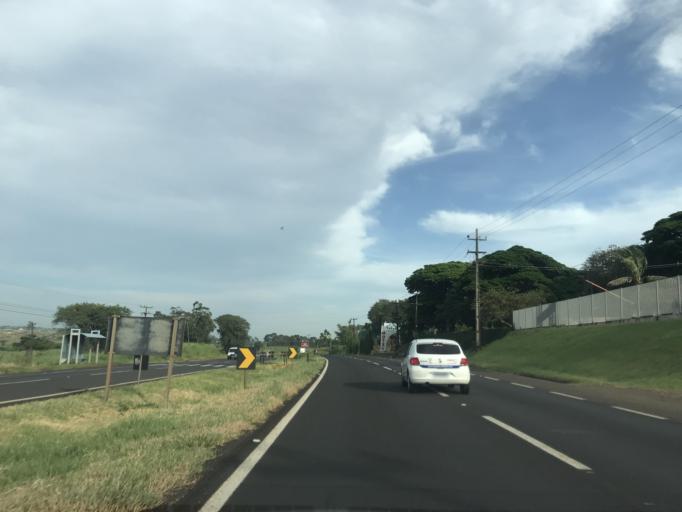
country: BR
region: Parana
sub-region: Paicandu
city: Paicandu
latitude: -23.3916
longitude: -52.0120
